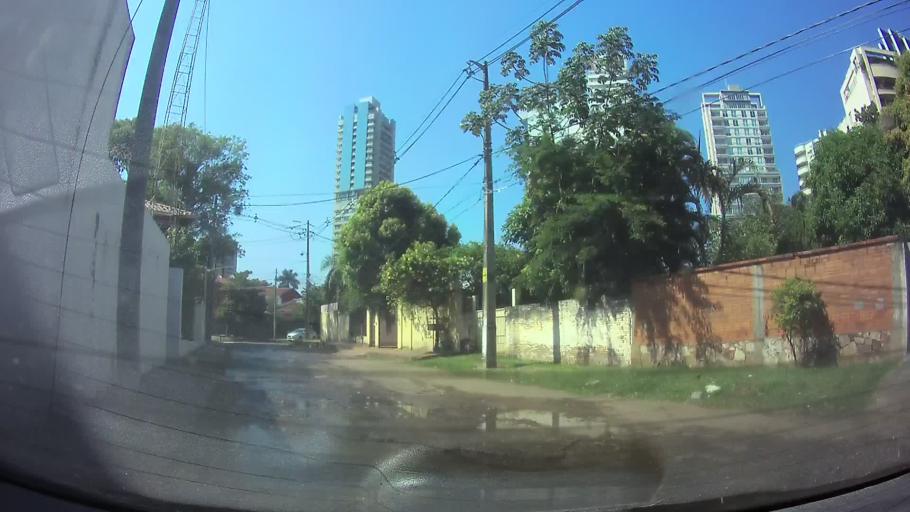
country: PY
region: Central
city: Fernando de la Mora
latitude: -25.2835
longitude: -57.5605
